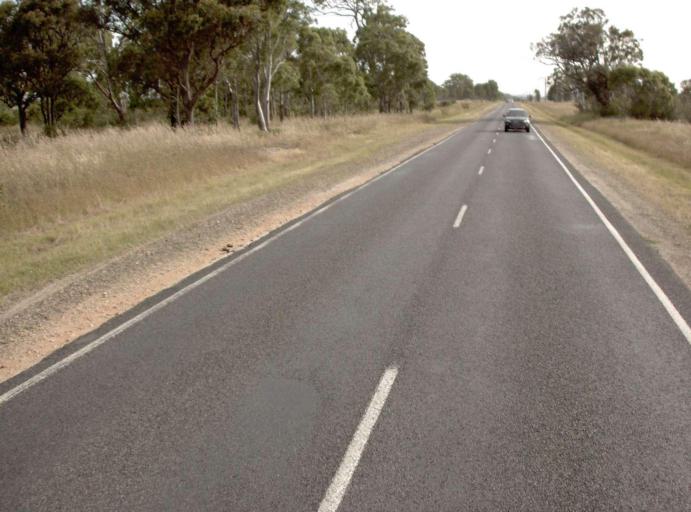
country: AU
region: Victoria
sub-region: Latrobe
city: Traralgon
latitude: -38.0733
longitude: 146.6131
